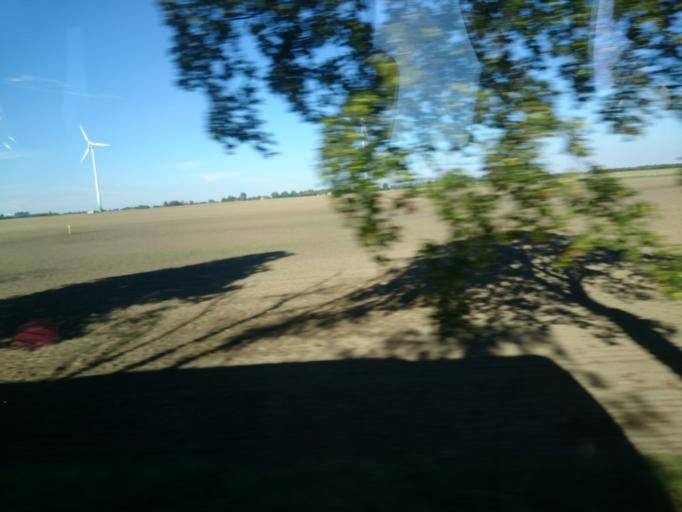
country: DE
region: Mecklenburg-Vorpommern
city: Anklam
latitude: 53.9077
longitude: 13.6576
